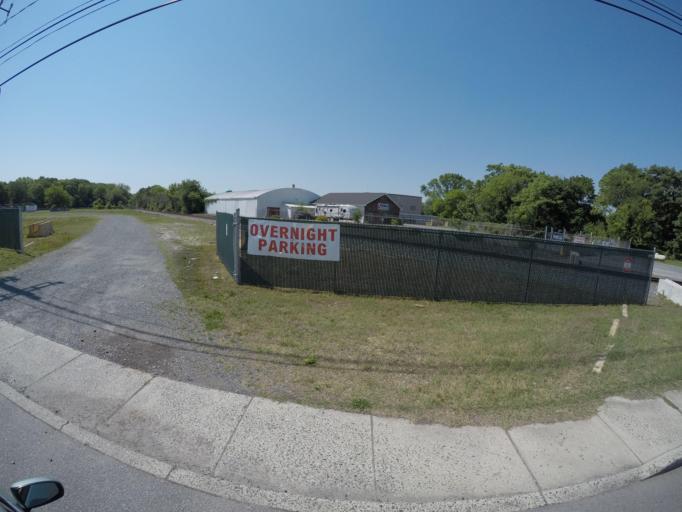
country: US
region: Delaware
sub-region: Sussex County
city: Georgetown
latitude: 38.6908
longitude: -75.3795
